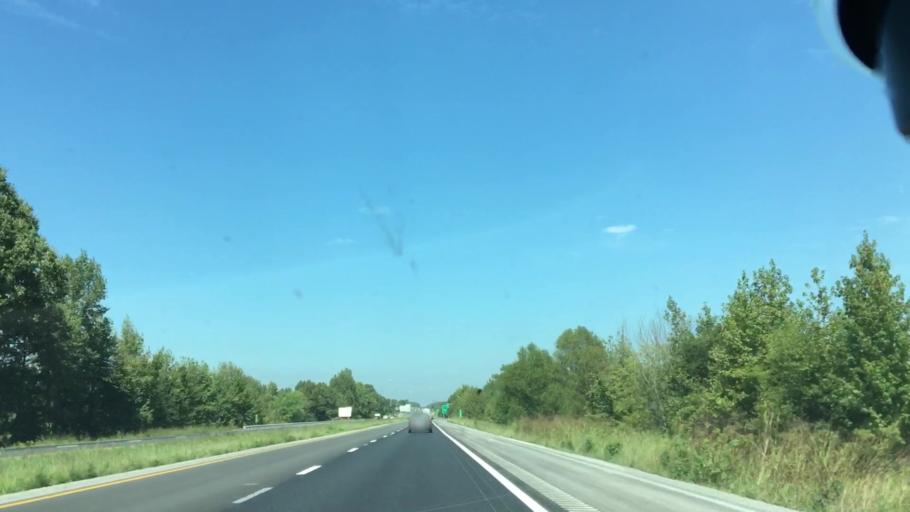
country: US
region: Kentucky
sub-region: Hopkins County
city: Nortonville
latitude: 37.2384
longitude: -87.4470
